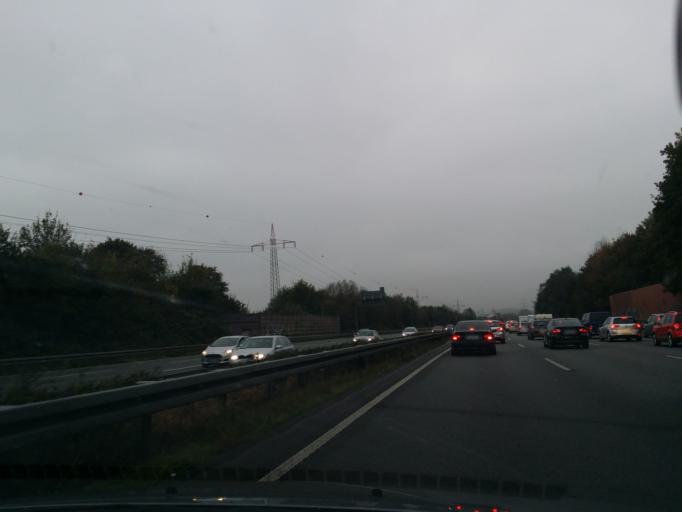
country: DE
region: North Rhine-Westphalia
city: Schwerte
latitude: 51.4664
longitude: 7.5915
